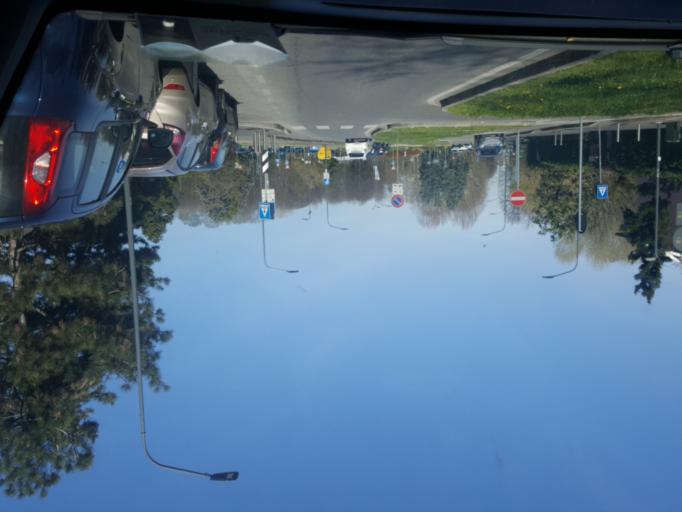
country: IT
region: Lombardy
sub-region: Citta metropolitana di Milano
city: Novate Milanese
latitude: 45.4855
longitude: 9.1387
